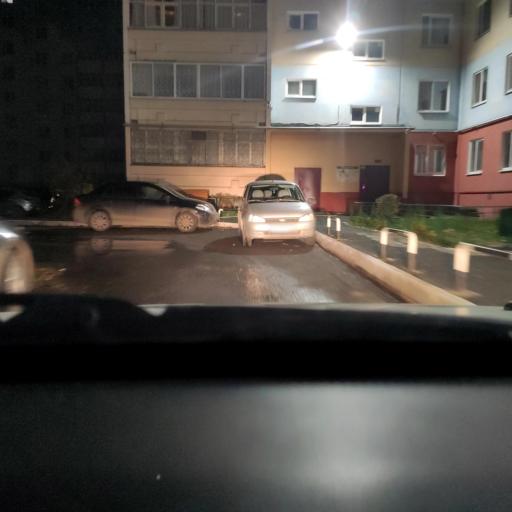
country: RU
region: Perm
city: Kondratovo
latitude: 58.0460
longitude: 56.0827
